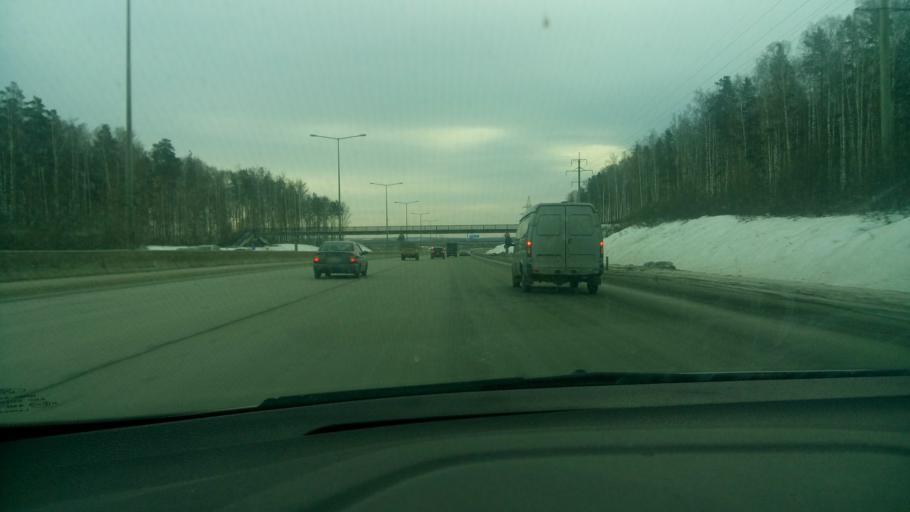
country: RU
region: Sverdlovsk
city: Istok
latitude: 56.7705
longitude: 60.7291
